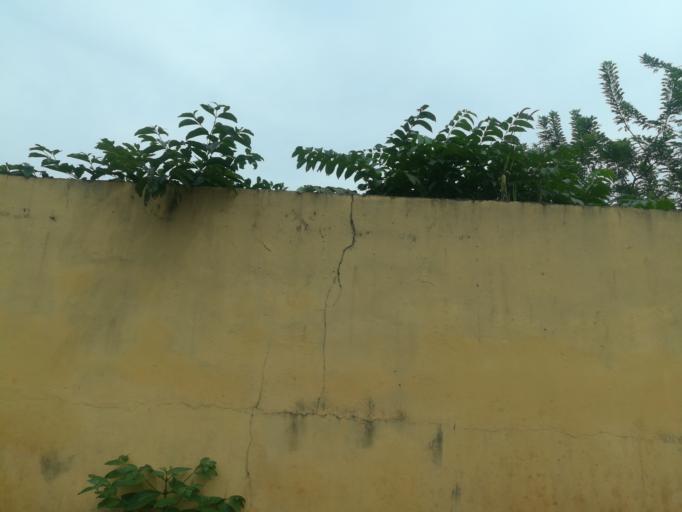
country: NG
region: Oyo
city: Ibadan
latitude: 7.4255
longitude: 3.9205
